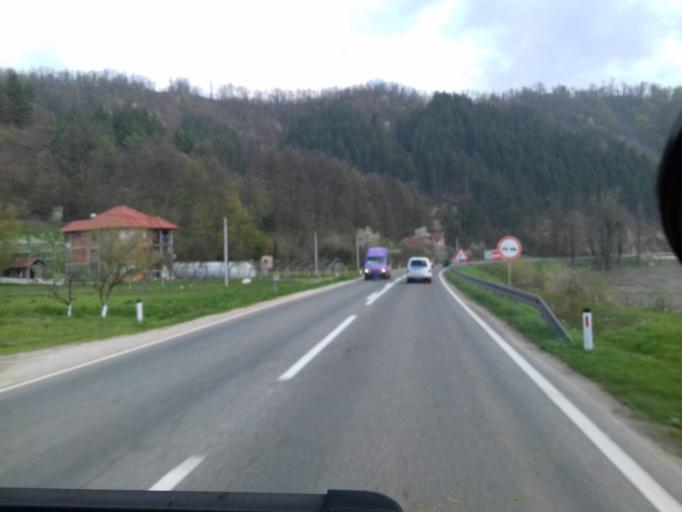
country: BA
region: Federation of Bosnia and Herzegovina
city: Maglaj
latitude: 44.6031
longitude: 18.0874
